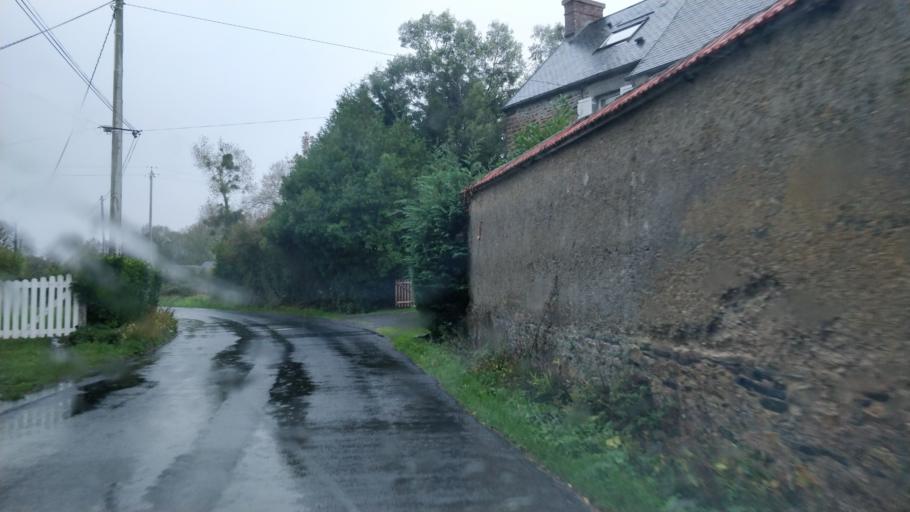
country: FR
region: Lower Normandy
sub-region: Departement de la Manche
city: Brehal
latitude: 48.9023
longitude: -1.5402
